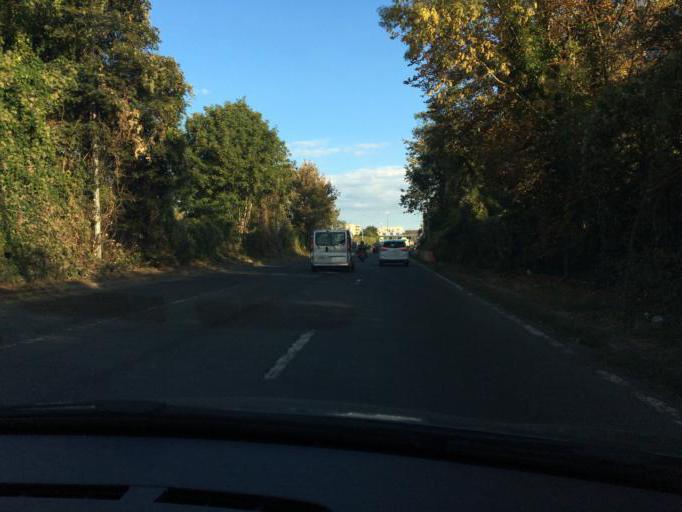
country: FR
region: Ile-de-France
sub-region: Departement de Seine-Saint-Denis
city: Montreuil
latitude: 48.8649
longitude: 2.4609
